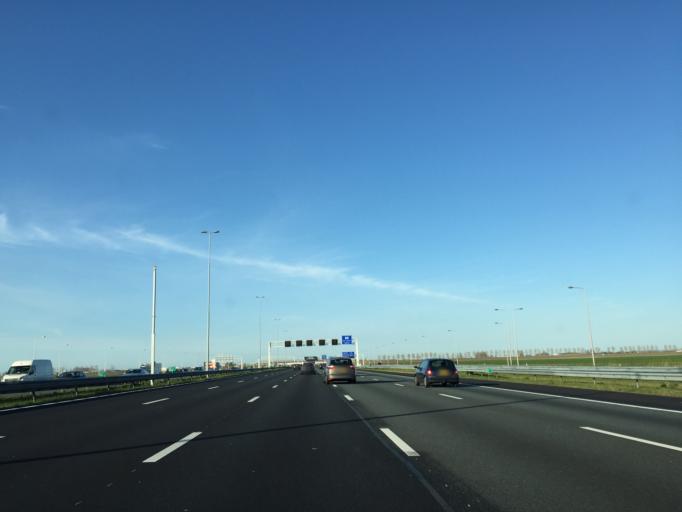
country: NL
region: North Holland
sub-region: Gemeente Haarlemmermeer
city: Hoofddorp
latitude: 52.2739
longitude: 4.7064
